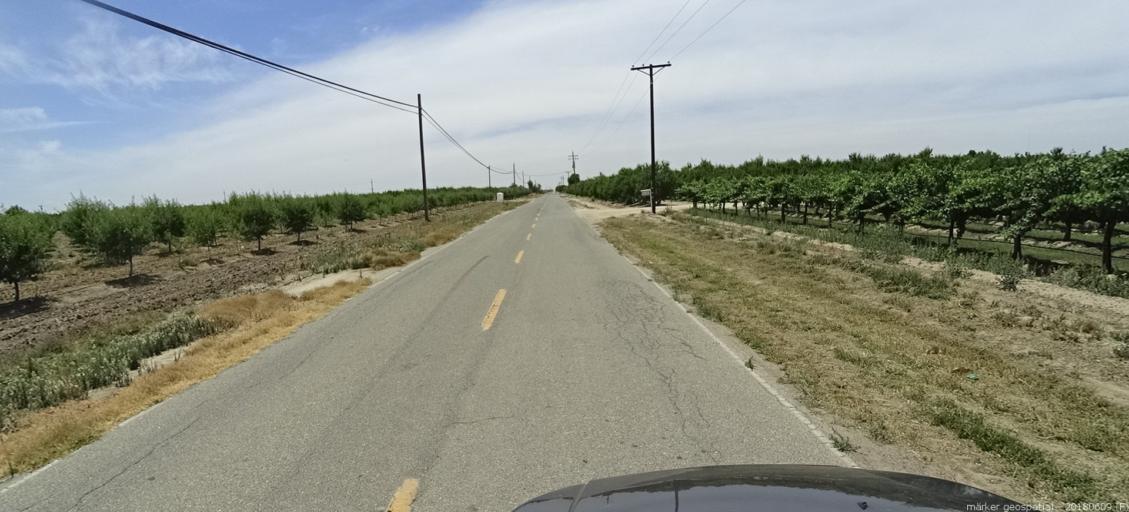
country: US
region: California
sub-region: Madera County
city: Parkwood
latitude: 36.9093
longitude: -120.1066
